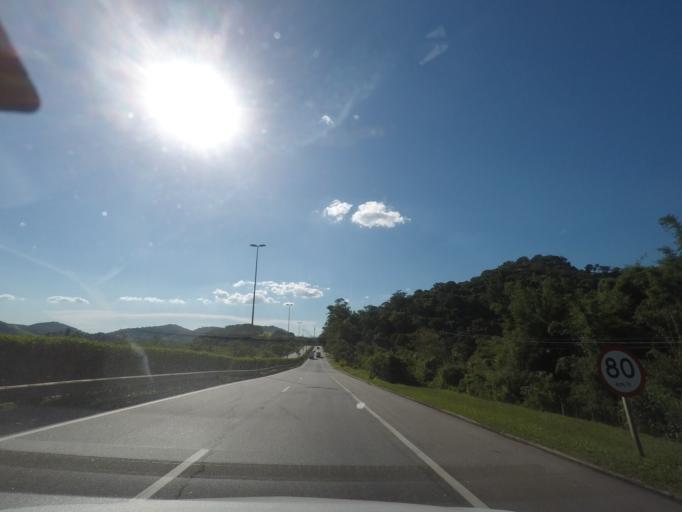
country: BR
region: Rio de Janeiro
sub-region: Sao Goncalo
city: Sao Goncalo
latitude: -22.6650
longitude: -43.1084
